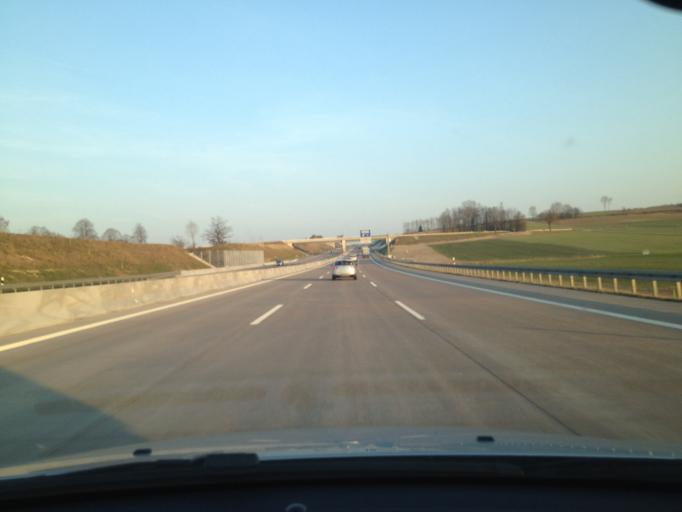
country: DE
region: Bavaria
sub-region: Swabia
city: Burgau
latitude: 48.4290
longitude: 10.3763
